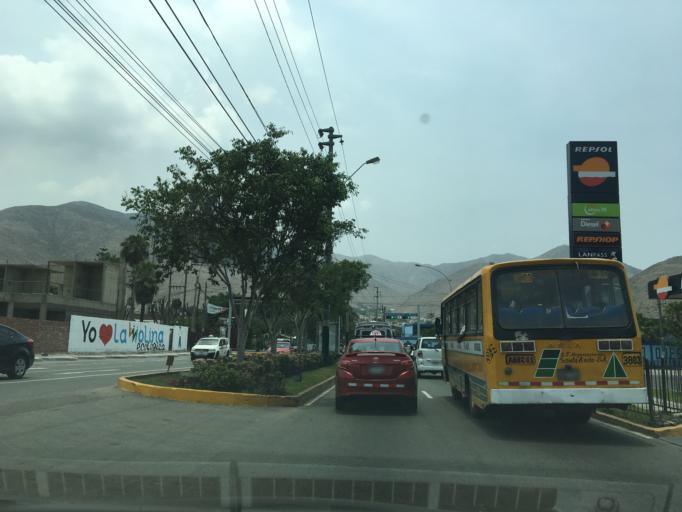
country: PE
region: Lima
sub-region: Lima
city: La Molina
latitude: -12.0835
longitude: -76.9278
